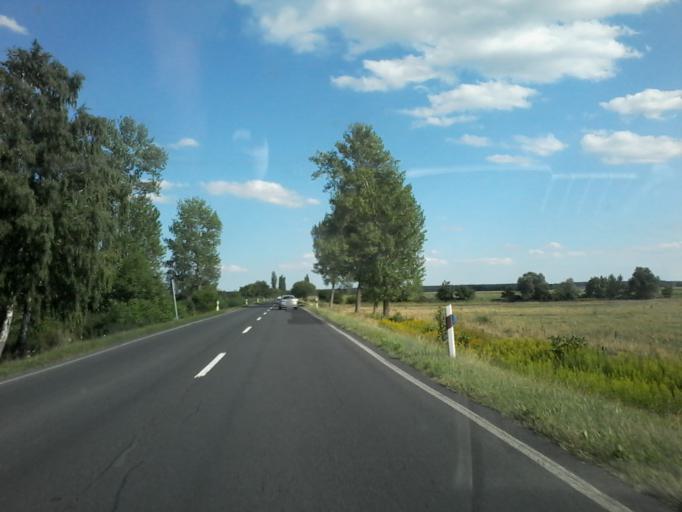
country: HU
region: Vas
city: Janoshaza
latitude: 47.1271
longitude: 17.1188
